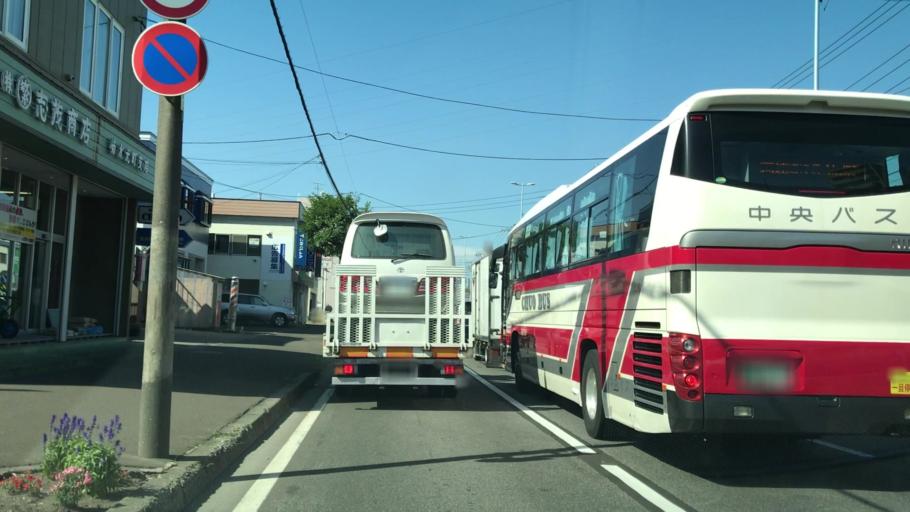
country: JP
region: Hokkaido
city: Sapporo
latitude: 43.0731
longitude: 141.4099
